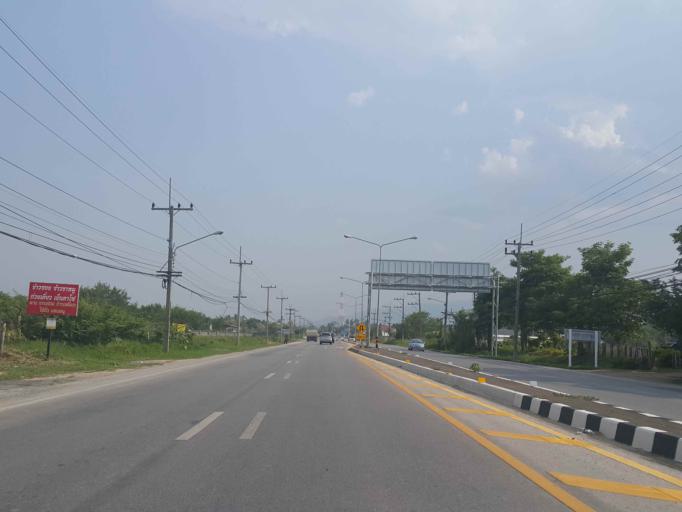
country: TH
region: Chiang Mai
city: Mae Taeng
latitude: 19.0245
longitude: 98.9448
